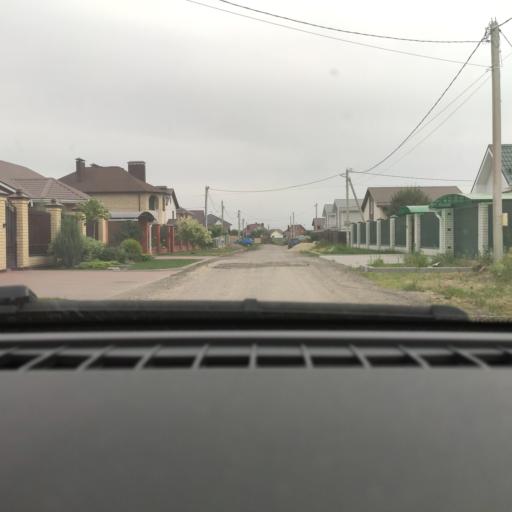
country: RU
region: Voronezj
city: Novaya Usman'
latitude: 51.6479
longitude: 39.3395
